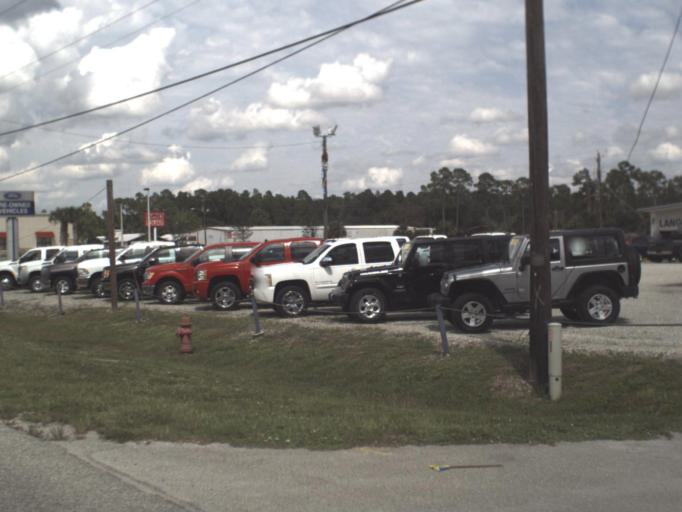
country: US
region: Florida
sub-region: Hendry County
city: LaBelle
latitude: 26.7492
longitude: -81.4380
